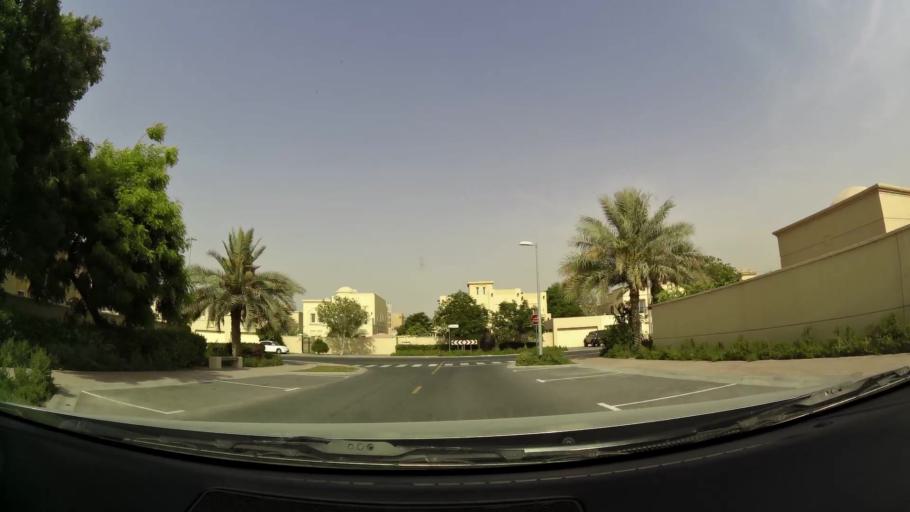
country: AE
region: Ash Shariqah
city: Sharjah
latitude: 25.2674
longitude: 55.4548
